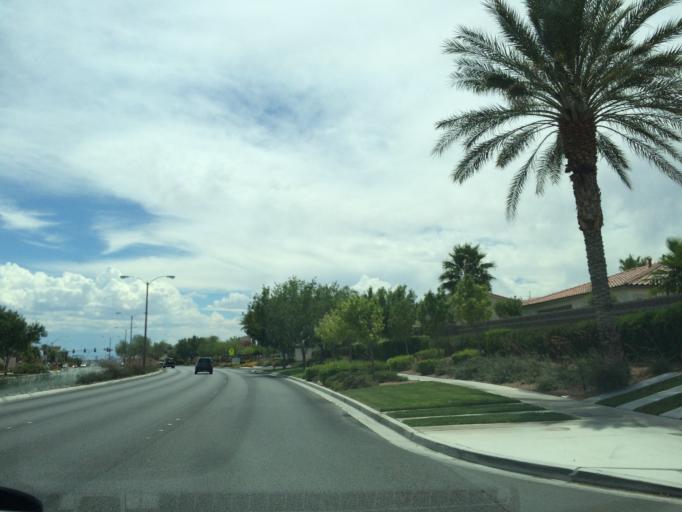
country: US
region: Nevada
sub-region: Clark County
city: North Las Vegas
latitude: 36.2788
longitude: -115.1797
